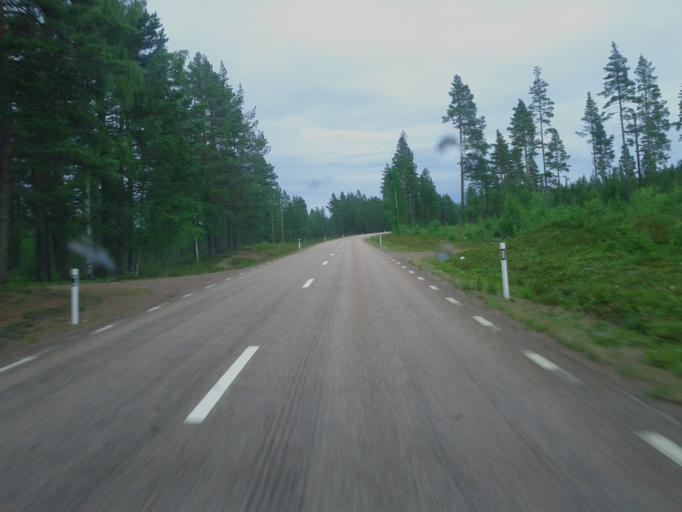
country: SE
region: Dalarna
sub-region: Mora Kommun
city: Mora
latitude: 61.0709
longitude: 14.3754
